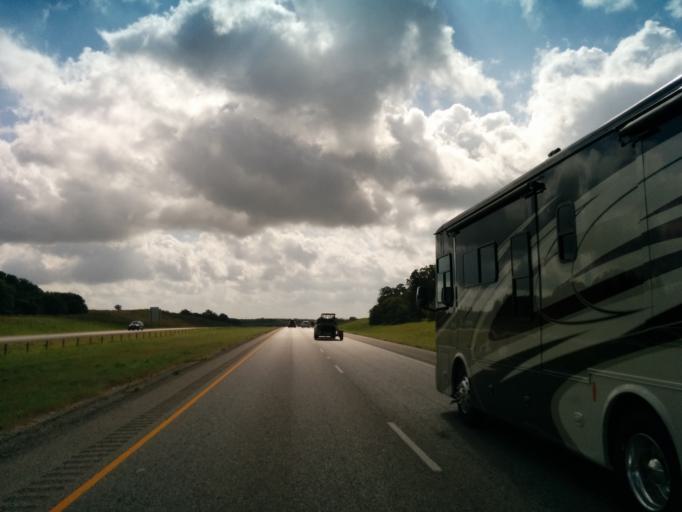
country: US
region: Texas
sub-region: Gonzales County
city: Waelder
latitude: 29.6607
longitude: -97.3963
